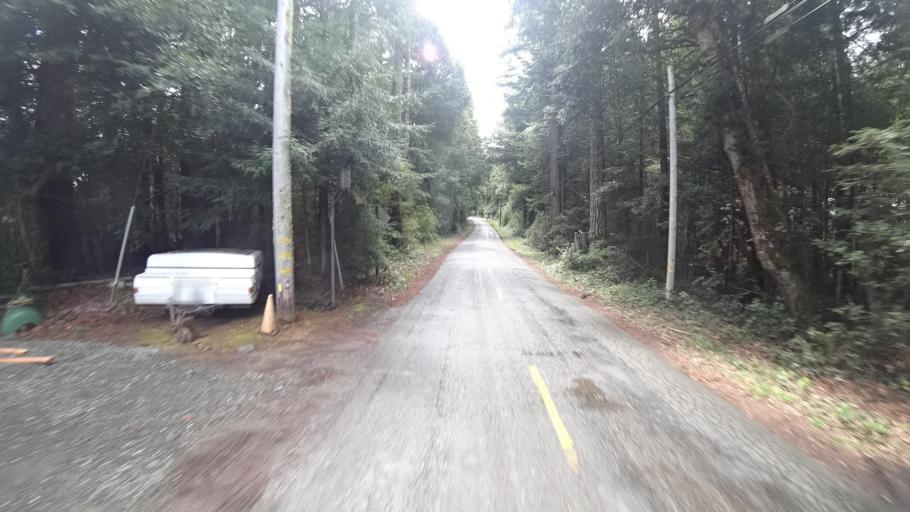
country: US
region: California
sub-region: Humboldt County
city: Bayside
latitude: 40.7733
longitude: -124.0016
